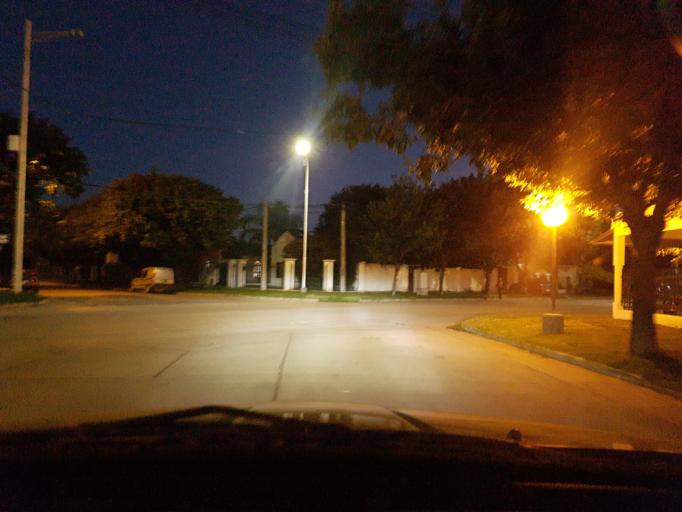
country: AR
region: Cordoba
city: Las Perdices
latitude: -32.7571
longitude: -63.7791
